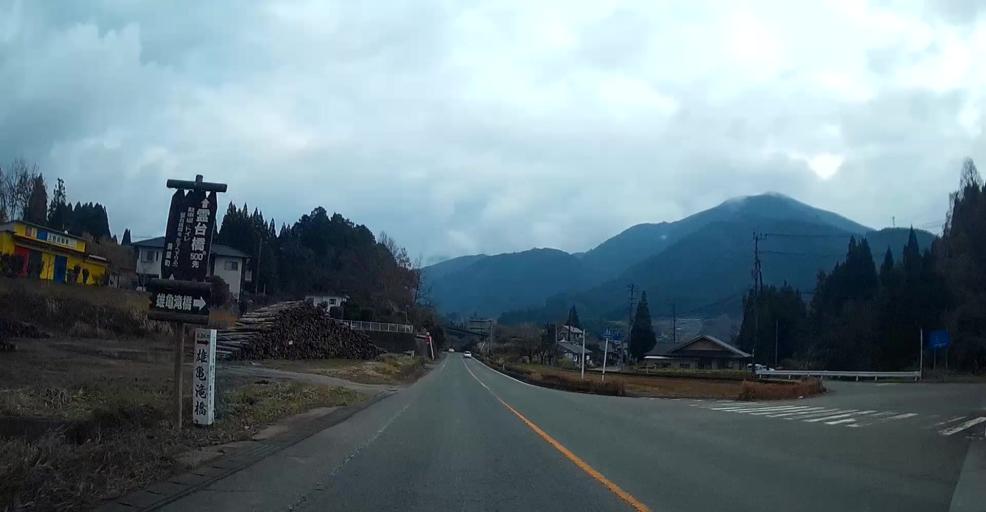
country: JP
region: Kumamoto
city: Matsubase
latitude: 32.6240
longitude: 130.8786
